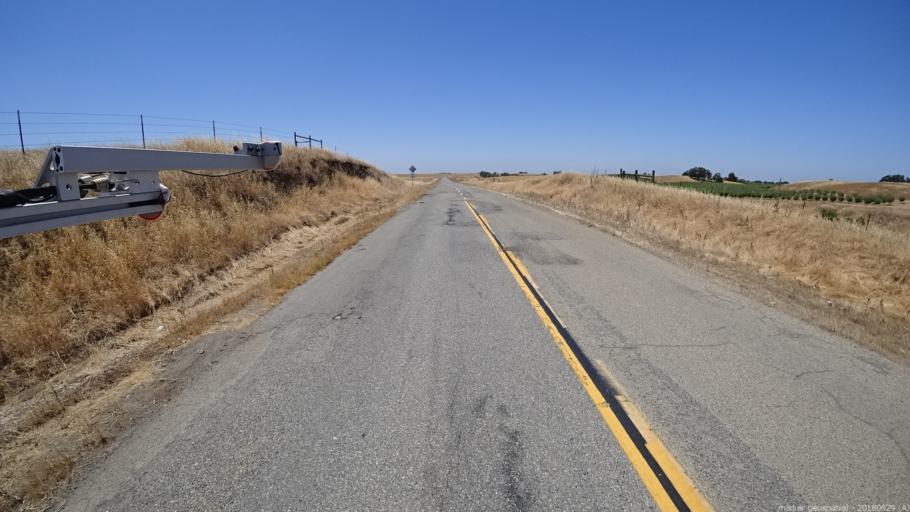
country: US
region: California
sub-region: Madera County
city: Bonadelle Ranchos-Madera Ranchos
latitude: 37.0578
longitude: -119.9101
